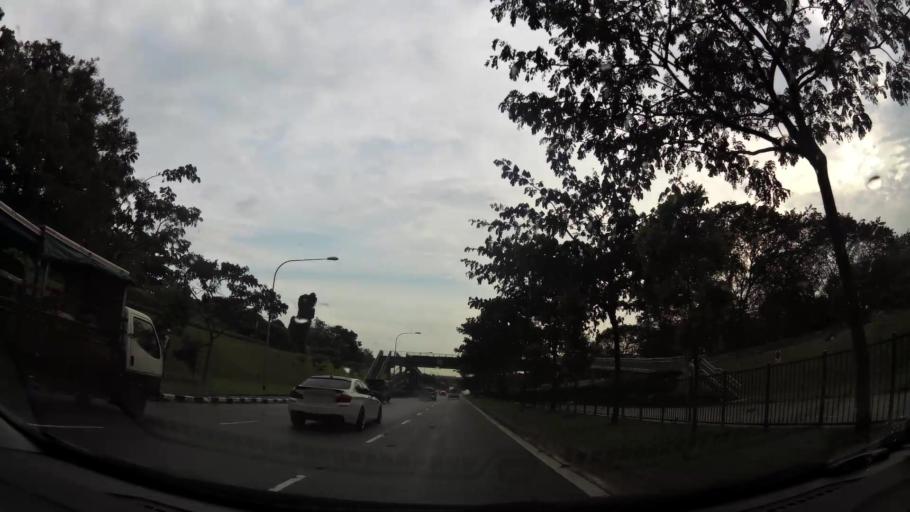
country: MY
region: Johor
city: Kampung Pasir Gudang Baru
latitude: 1.3982
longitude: 103.8690
